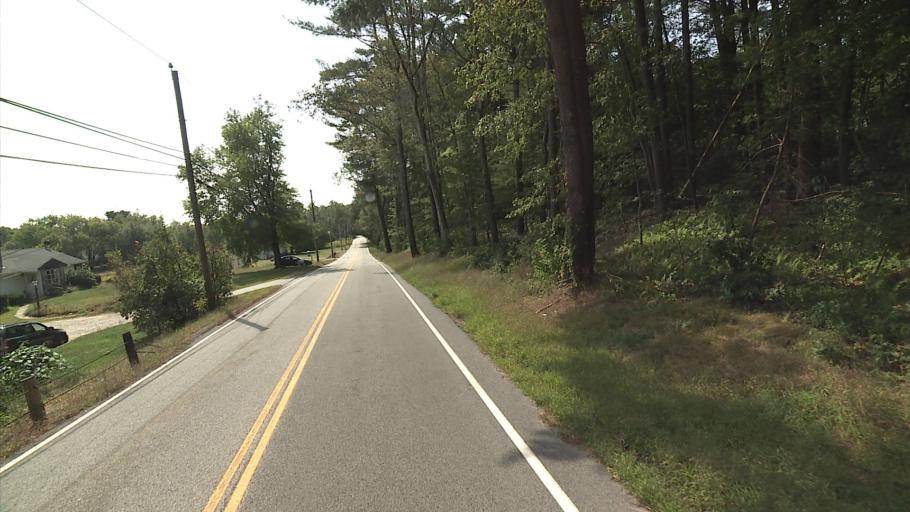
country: US
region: Connecticut
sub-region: Windham County
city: Wauregan
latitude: 41.7709
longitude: -71.9550
